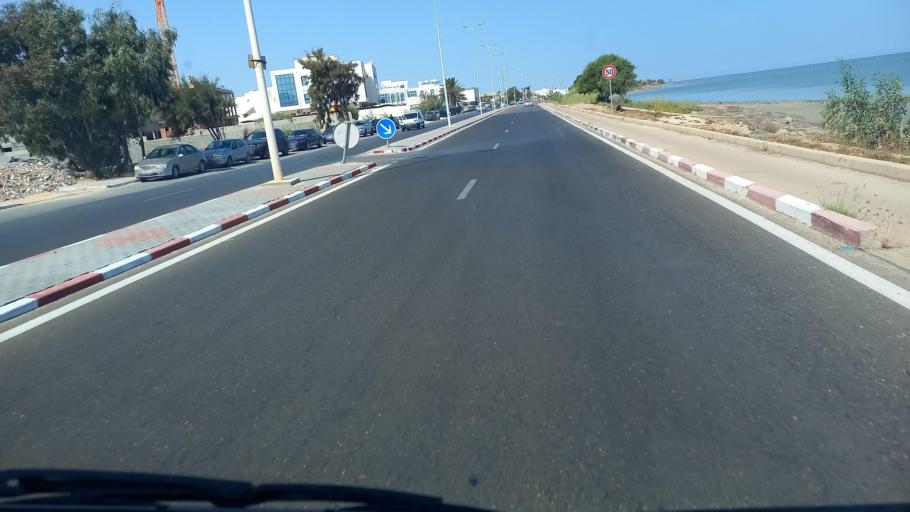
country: TN
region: Madanin
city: Houmt Souk
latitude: 33.8747
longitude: 10.8939
